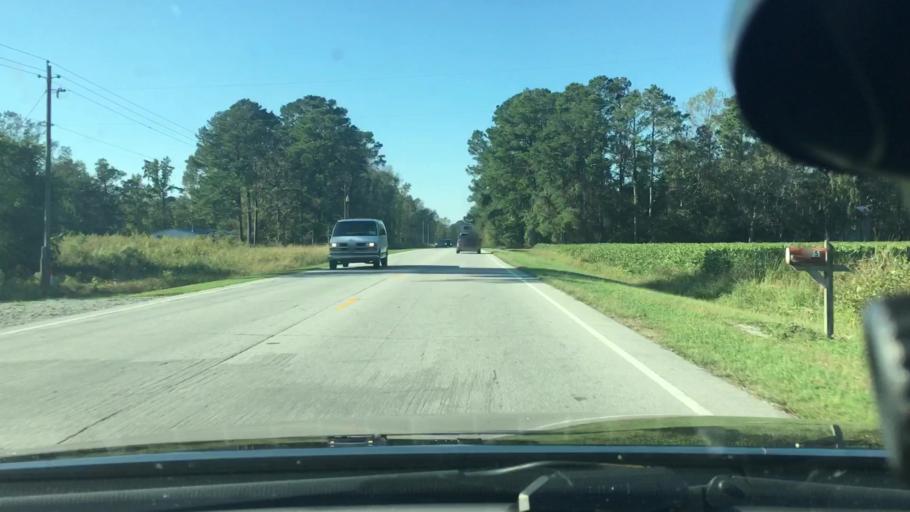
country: US
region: North Carolina
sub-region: Craven County
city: Vanceboro
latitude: 35.2738
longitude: -77.1152
